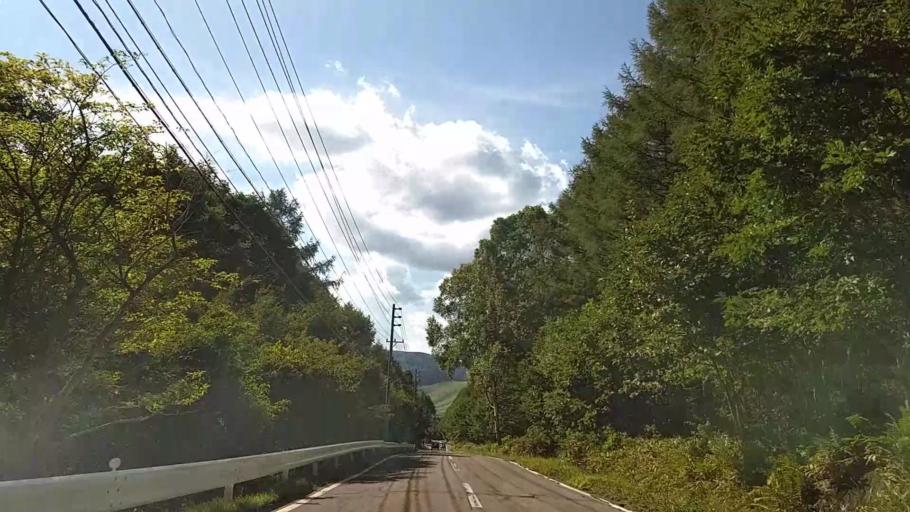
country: JP
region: Nagano
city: Chino
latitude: 36.1000
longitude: 138.2531
